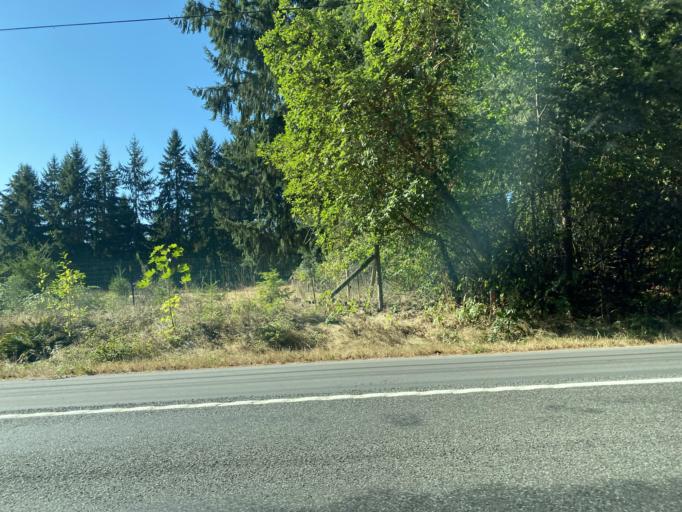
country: US
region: Washington
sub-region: Thurston County
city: Tanglewilde-Thompson Place
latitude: 46.9856
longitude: -122.7488
